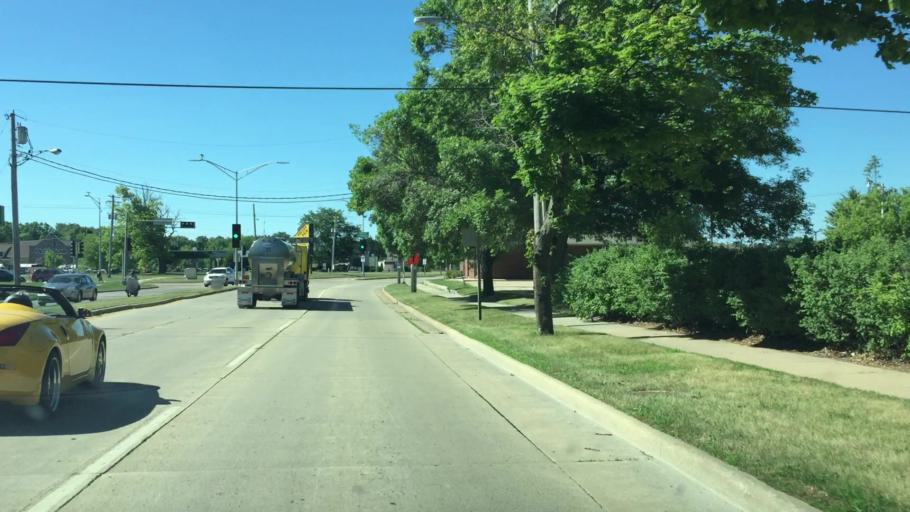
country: US
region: Wisconsin
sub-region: Outagamie County
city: Appleton
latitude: 44.2441
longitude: -88.4157
